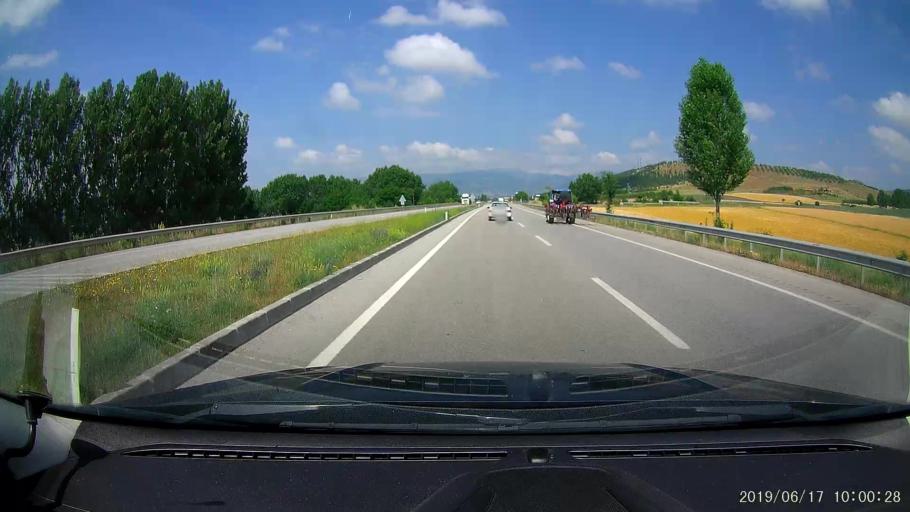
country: TR
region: Amasya
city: Alicik
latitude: 40.8664
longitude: 35.2876
